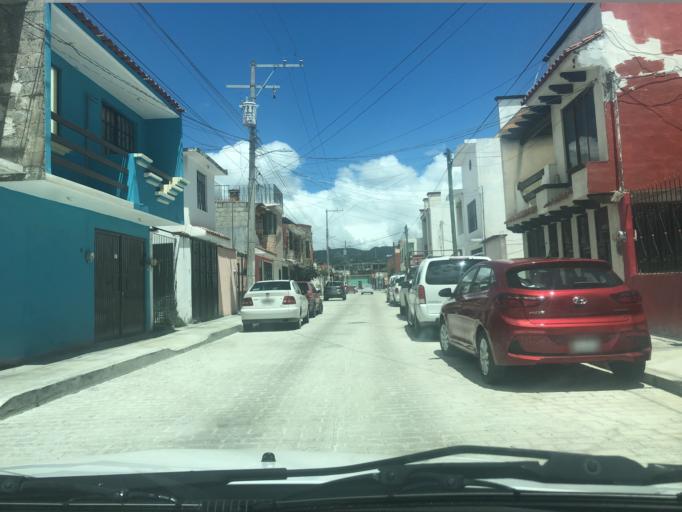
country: MX
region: Chiapas
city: San Cristobal de las Casas
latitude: 16.7166
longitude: -92.6449
